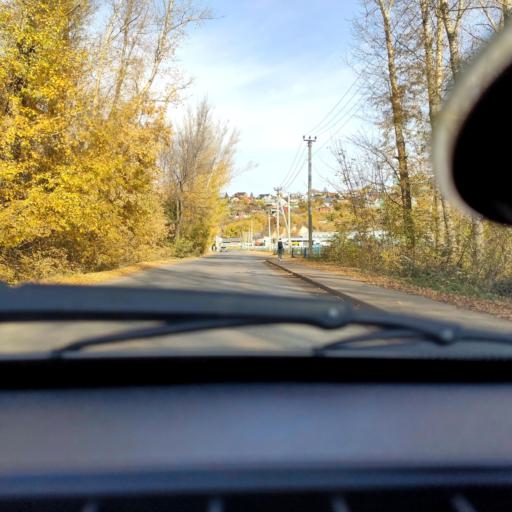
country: RU
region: Bashkortostan
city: Ufa
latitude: 54.6960
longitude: 55.9690
